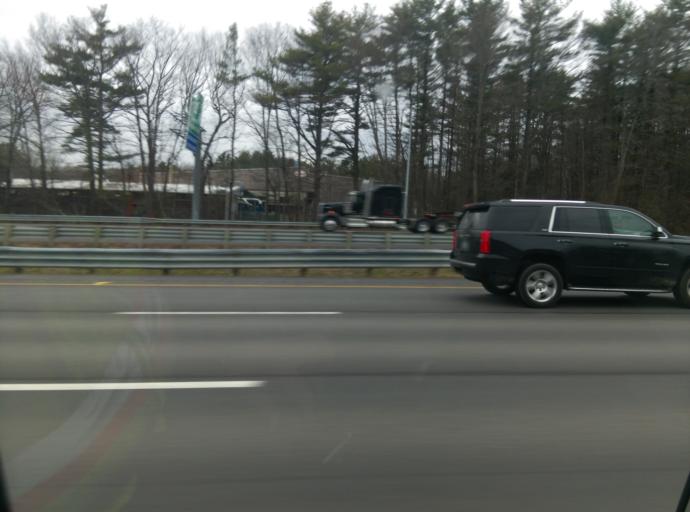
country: US
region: New Hampshire
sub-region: Rockingham County
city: Seabrook
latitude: 42.8835
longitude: -70.8821
